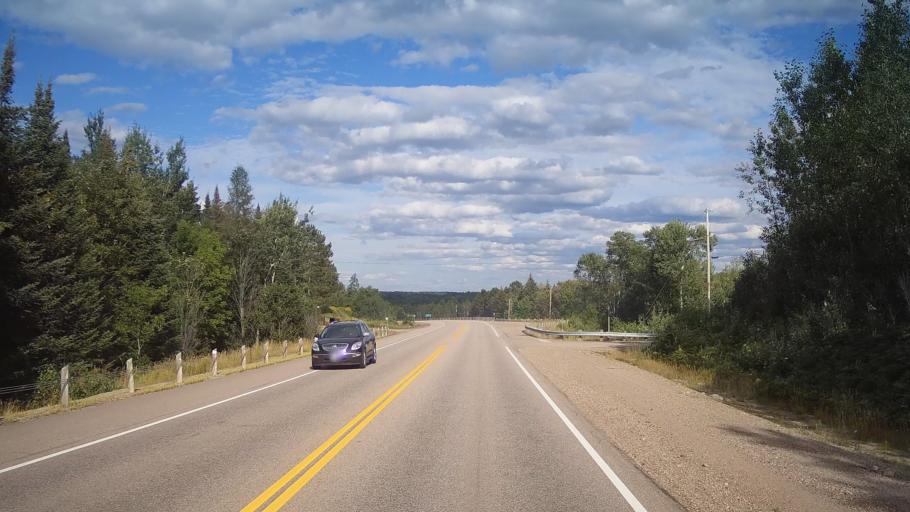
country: CA
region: Ontario
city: Mattawa
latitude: 46.2897
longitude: -78.7862
